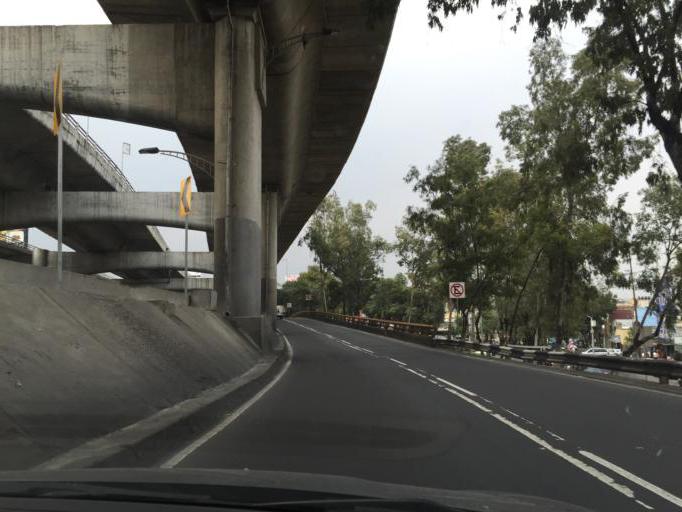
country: MX
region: Mexico City
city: Alvaro Obregon
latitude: 19.3718
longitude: -99.1915
